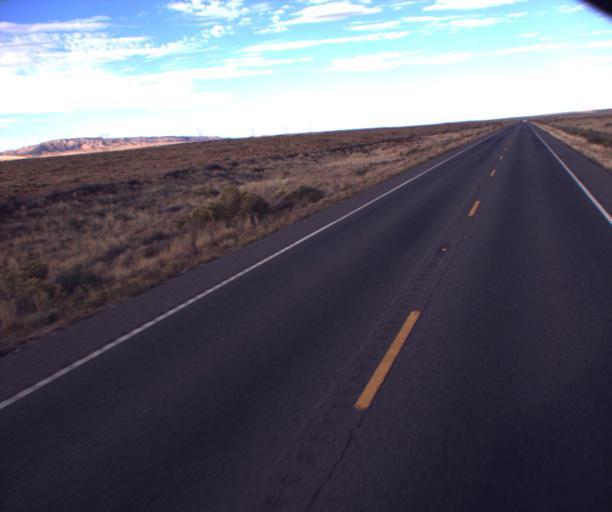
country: US
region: Arizona
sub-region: Apache County
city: Lukachukai
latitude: 36.9424
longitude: -109.2569
